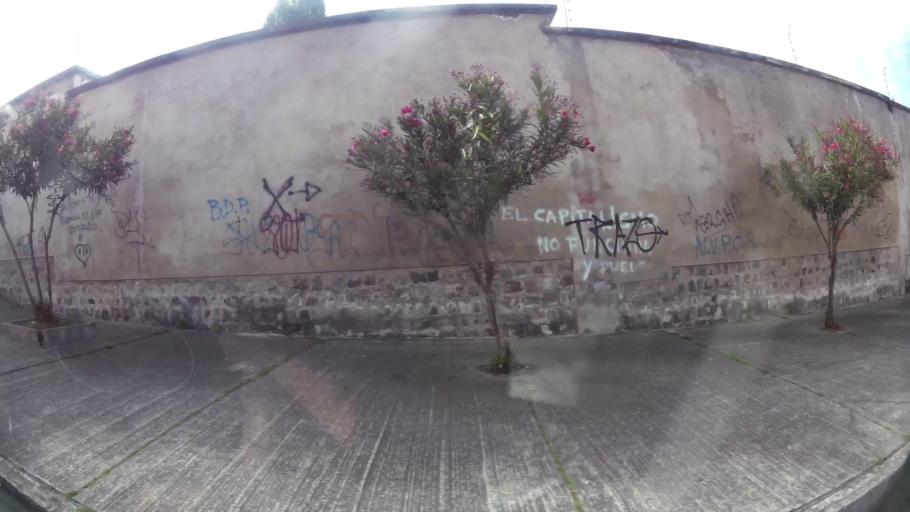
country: EC
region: Pichincha
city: Quito
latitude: -0.1620
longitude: -78.4699
